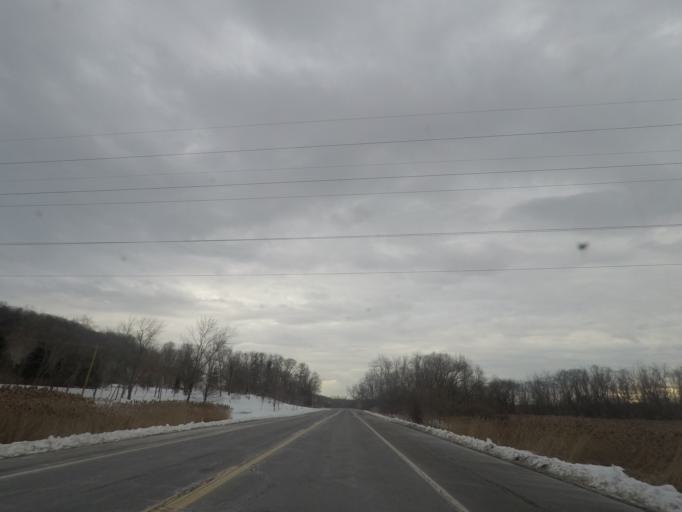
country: US
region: New York
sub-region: Rensselaer County
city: Hampton Manor
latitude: 42.5982
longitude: -73.7450
